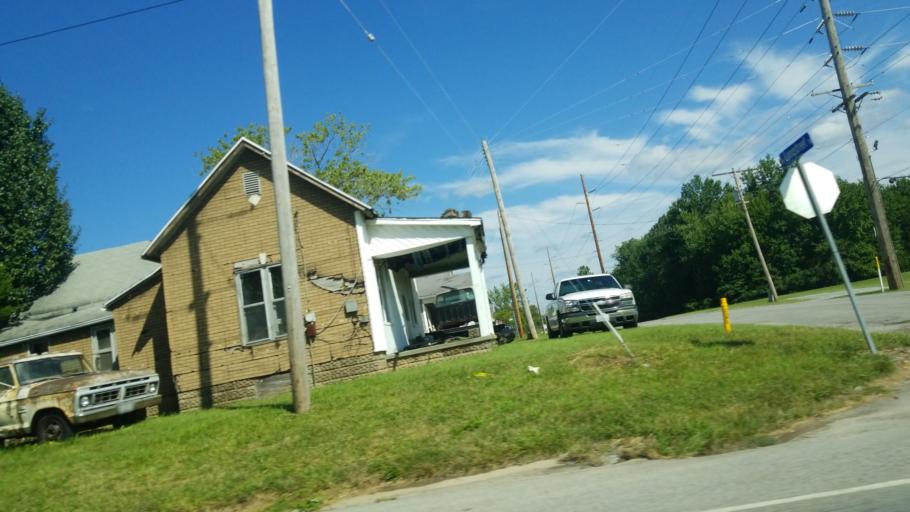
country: US
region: Illinois
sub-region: Williamson County
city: Marion
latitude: 37.7557
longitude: -88.9328
